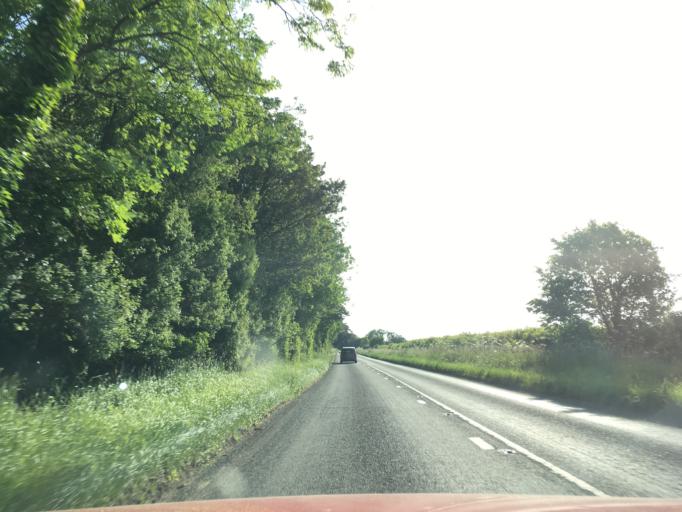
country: GB
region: England
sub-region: Gloucestershire
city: Fairford
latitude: 51.7036
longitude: -1.8096
